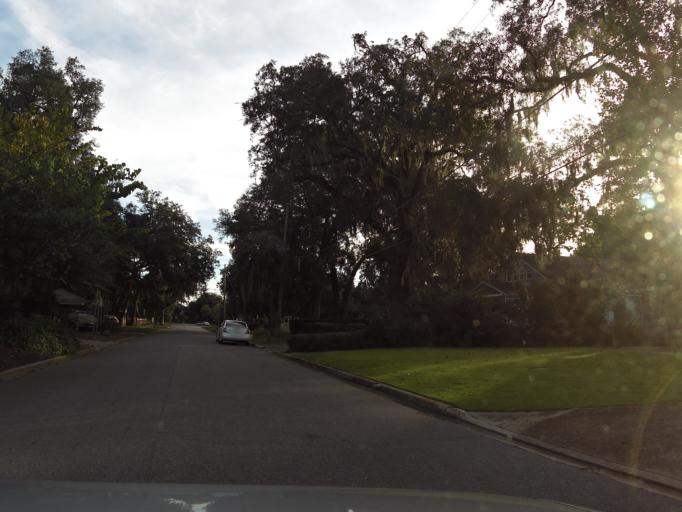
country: US
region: Florida
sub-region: Duval County
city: Jacksonville
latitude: 30.3905
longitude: -81.6611
